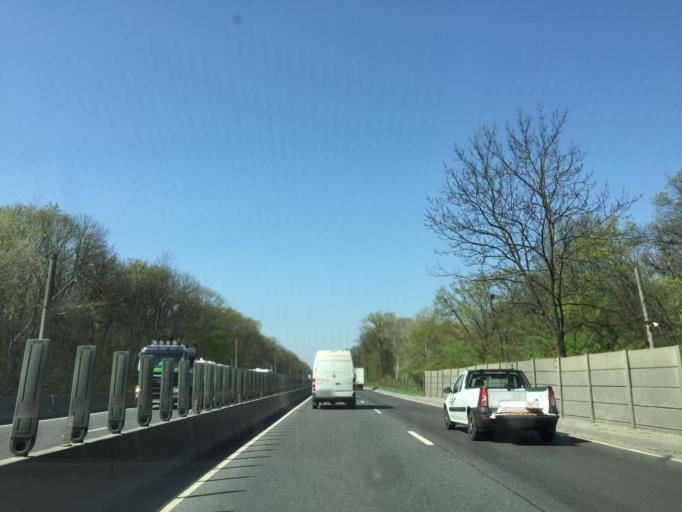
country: RO
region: Ilfov
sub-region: Comuna Tunari
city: Tunari
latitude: 44.5393
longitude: 26.1172
